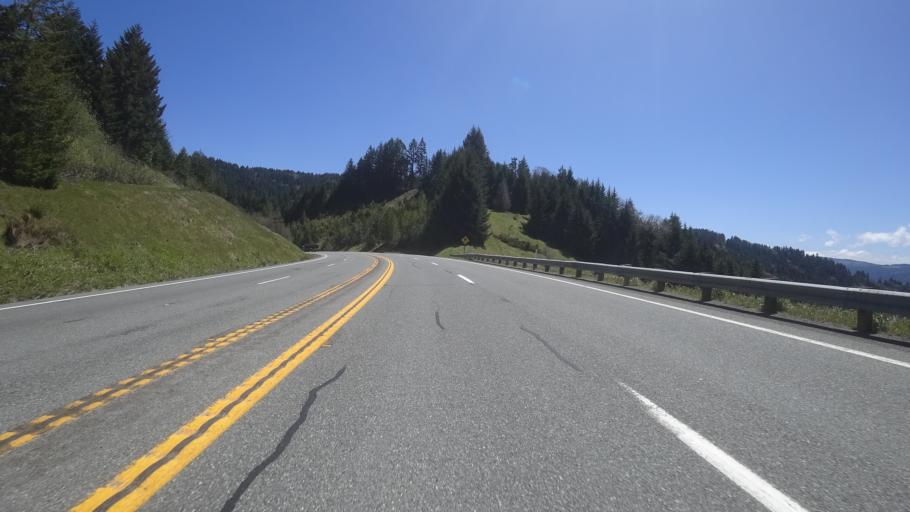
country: US
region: California
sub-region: Humboldt County
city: Willow Creek
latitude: 40.8969
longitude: -123.7732
